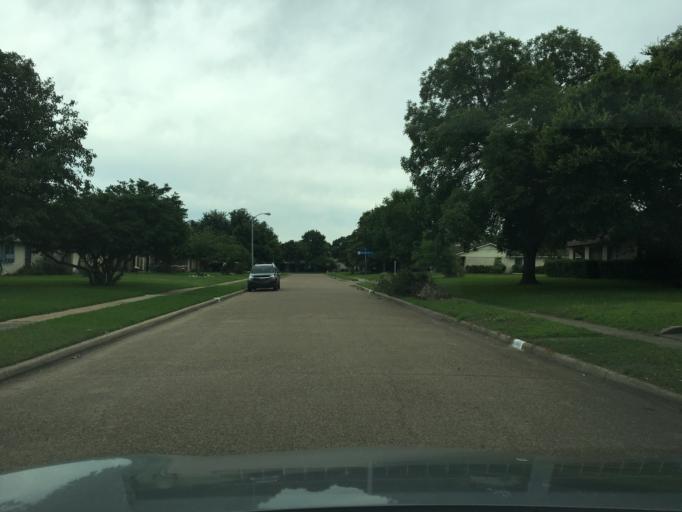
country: US
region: Texas
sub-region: Dallas County
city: Richardson
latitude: 32.9356
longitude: -96.7008
